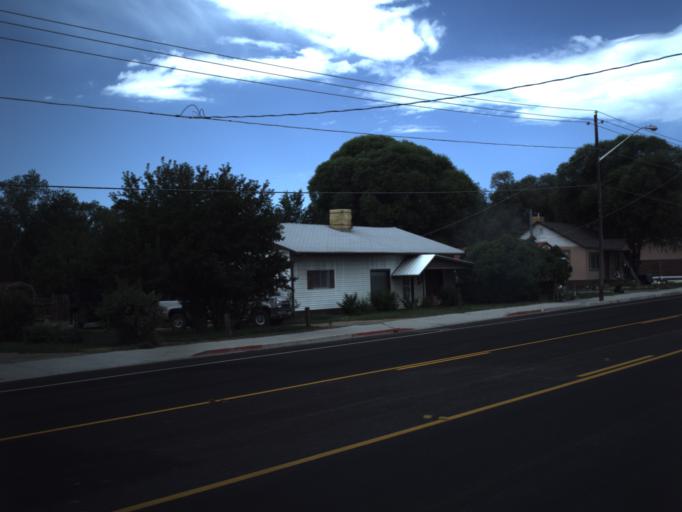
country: US
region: Utah
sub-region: Carbon County
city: Wellington
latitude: 39.5425
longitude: -110.7273
